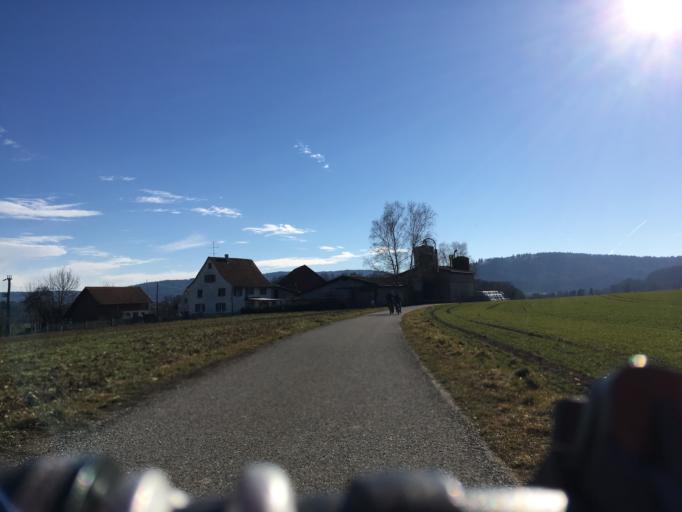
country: CH
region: Schaffhausen
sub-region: Bezirk Stein
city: Ramsen
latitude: 47.6901
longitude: 8.8130
